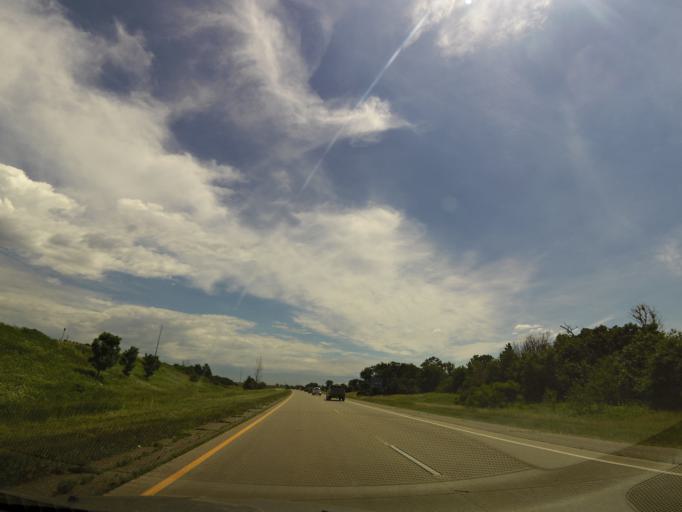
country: US
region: Minnesota
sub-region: Scott County
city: Prior Lake
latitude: 44.7829
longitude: -93.4244
